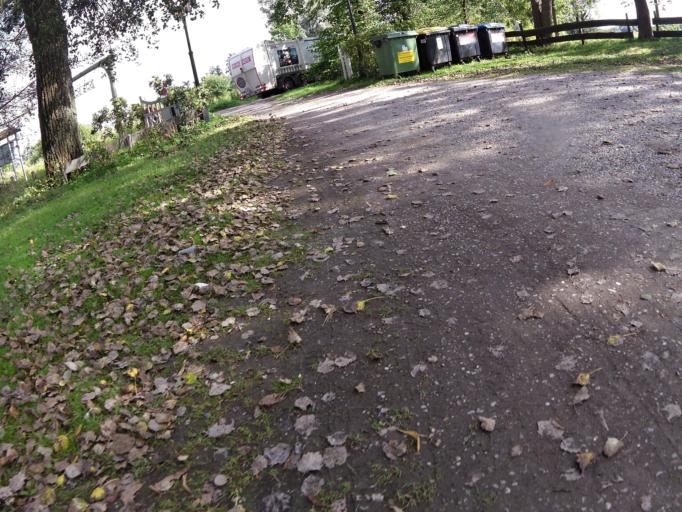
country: DE
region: Schleswig-Holstein
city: Wisch
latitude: 54.4167
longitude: 10.3735
